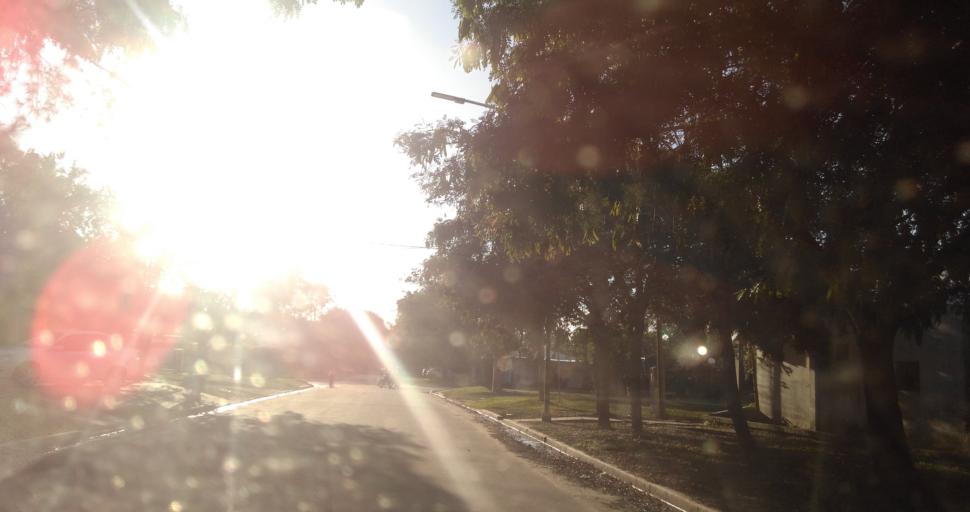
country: AR
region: Chaco
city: Colonia Benitez
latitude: -27.3322
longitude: -58.9452
